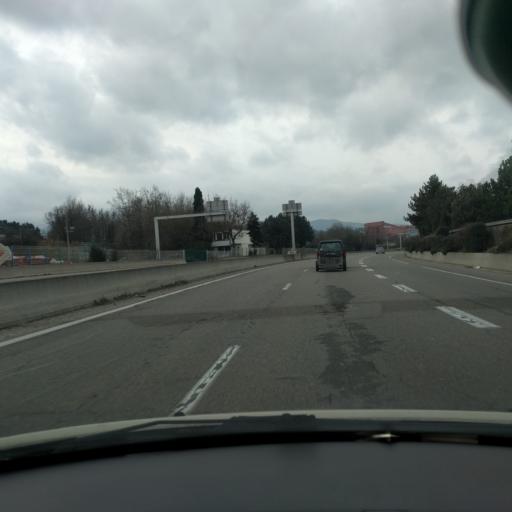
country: FR
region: Provence-Alpes-Cote d'Azur
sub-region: Departement des Bouches-du-Rhone
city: Gardanne
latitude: 43.4610
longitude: 5.4659
